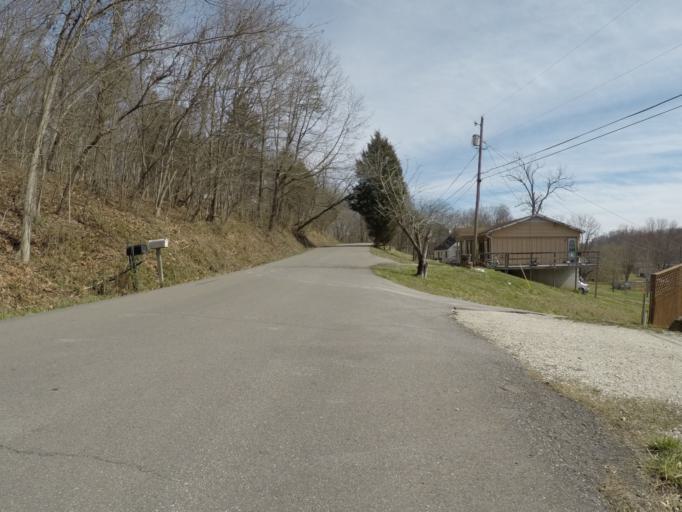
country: US
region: West Virginia
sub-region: Wayne County
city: Ceredo
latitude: 38.3736
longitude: -82.5450
